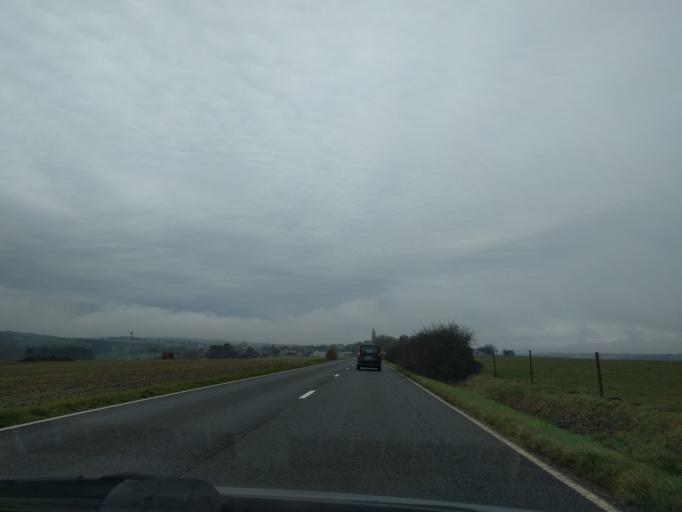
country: BE
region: Wallonia
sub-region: Province de Namur
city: Hastiere-Lavaux
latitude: 50.2407
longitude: 4.7734
